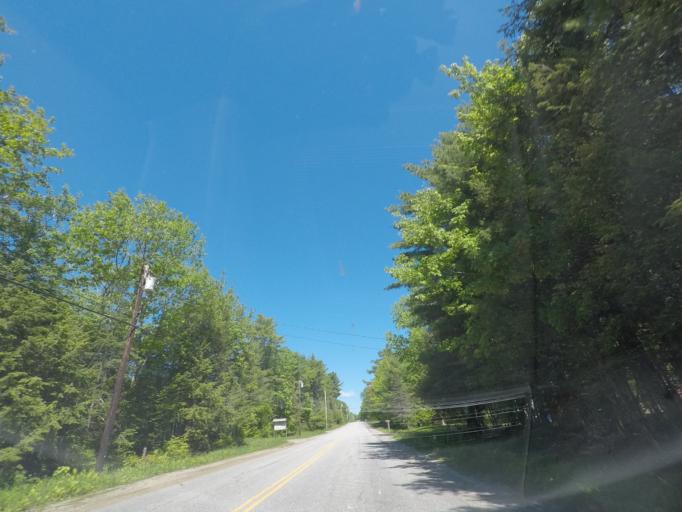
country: US
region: Maine
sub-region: Kennebec County
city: Manchester
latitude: 44.2299
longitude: -69.8796
